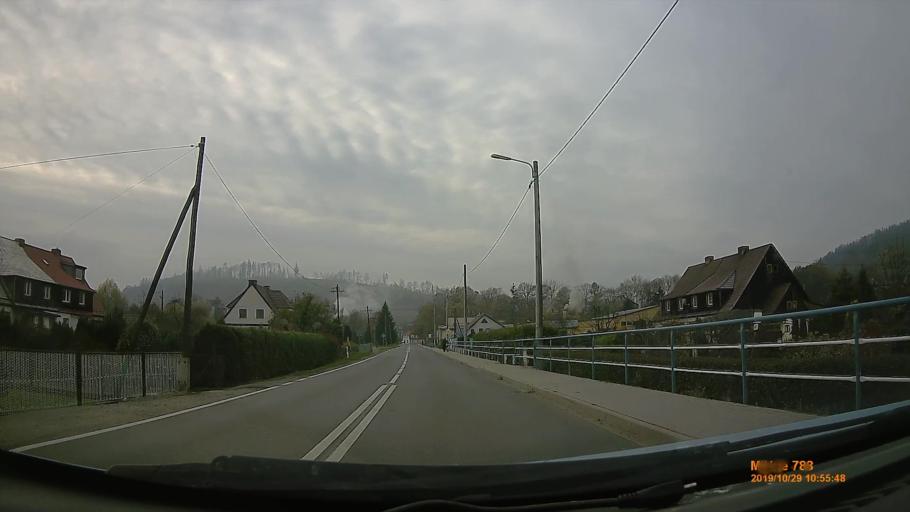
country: PL
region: Lower Silesian Voivodeship
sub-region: Powiat klodzki
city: Nowa Ruda
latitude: 50.5184
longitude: 16.4919
